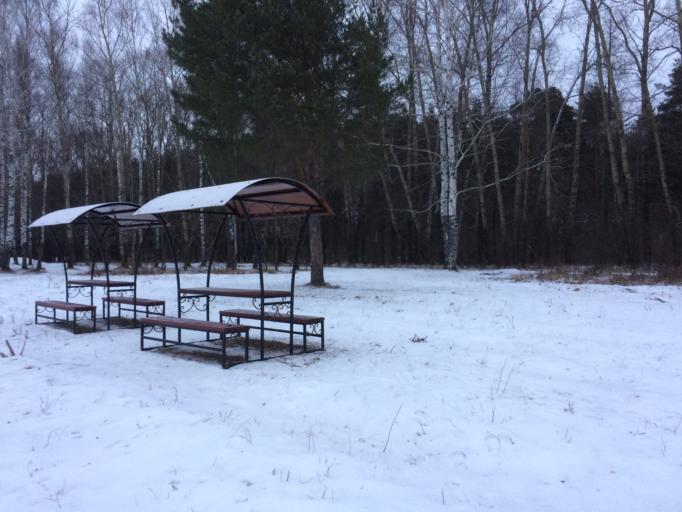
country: RU
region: Mariy-El
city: Yoshkar-Ola
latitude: 56.6218
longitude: 47.9171
